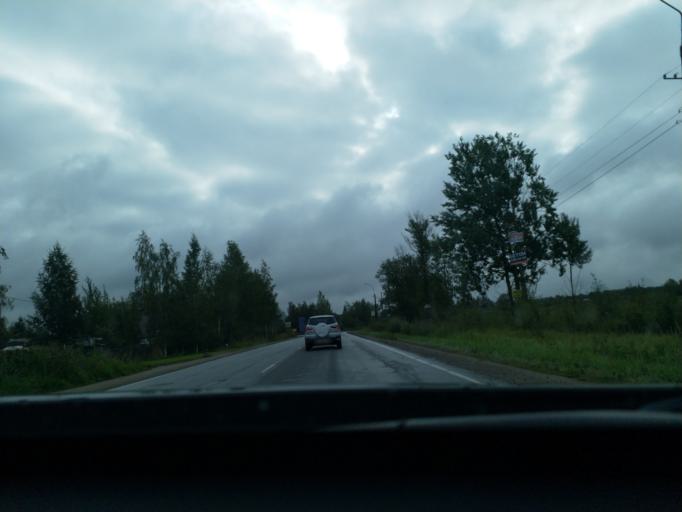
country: RU
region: Leningrad
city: Nikol'skoye
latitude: 59.6921
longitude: 30.7983
